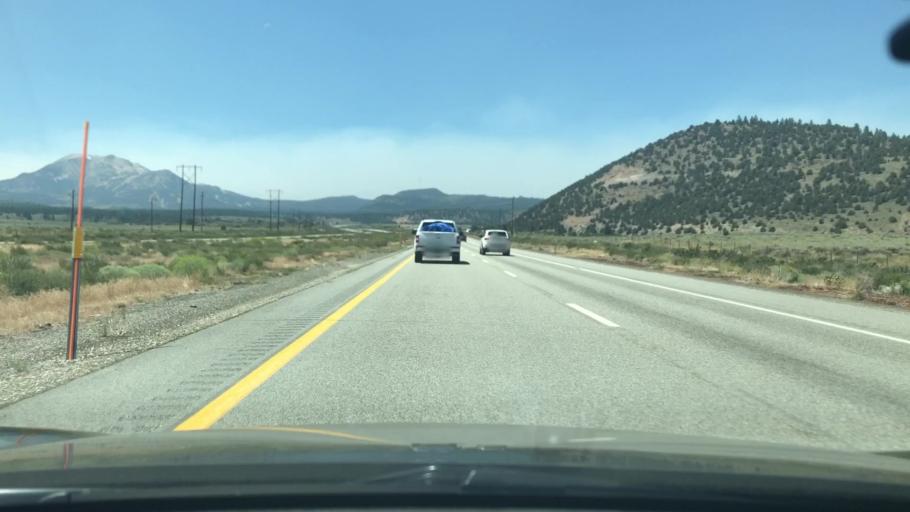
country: US
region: California
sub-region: Mono County
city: Mammoth Lakes
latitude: 37.6345
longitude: -118.8810
